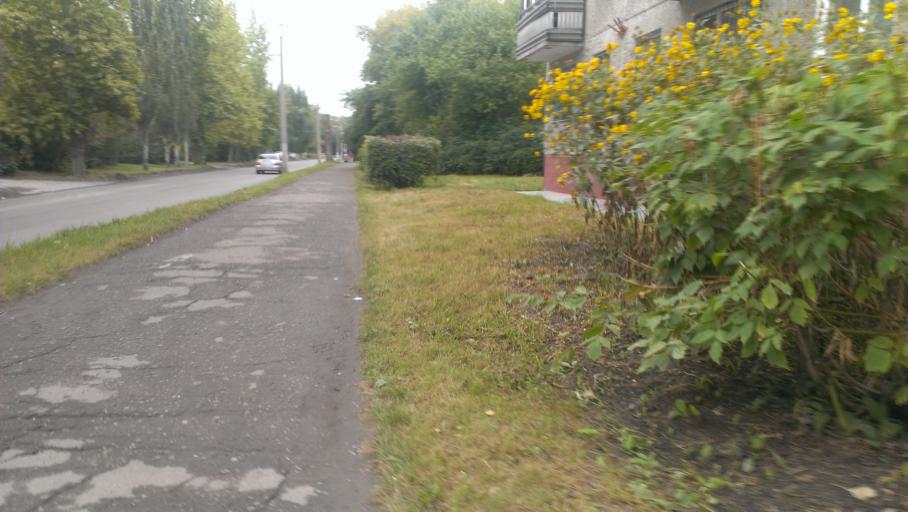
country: RU
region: Altai Krai
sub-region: Gorod Barnaulskiy
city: Barnaul
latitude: 53.3681
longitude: 83.6894
